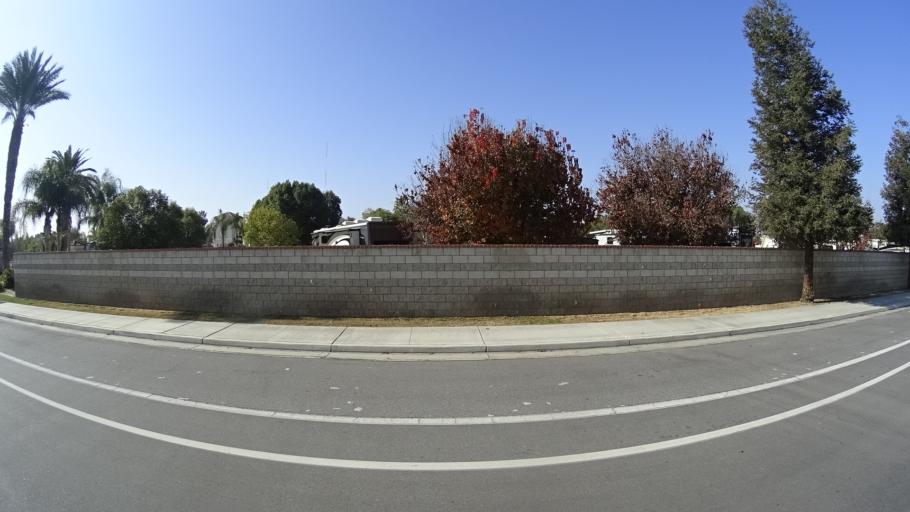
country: US
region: California
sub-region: Kern County
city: Greenfield
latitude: 35.3090
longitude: -119.0391
